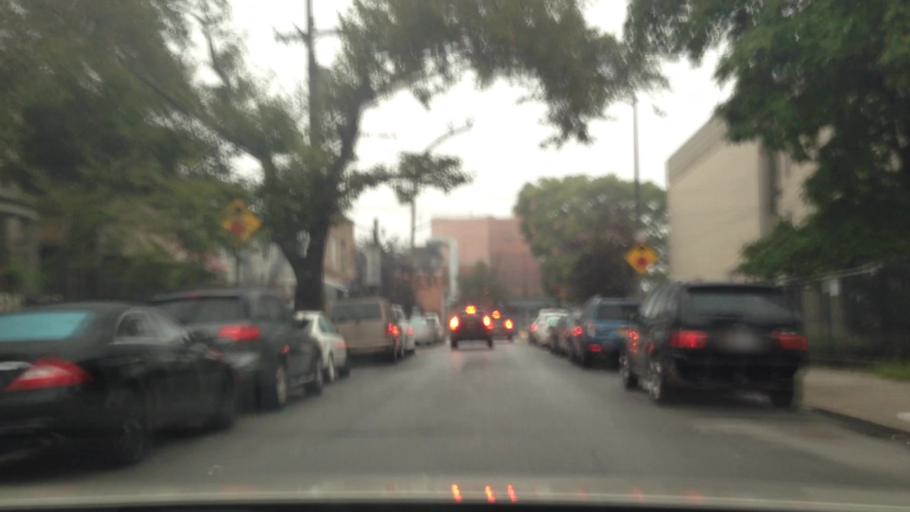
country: US
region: New York
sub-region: Kings County
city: East New York
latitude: 40.6641
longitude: -73.8861
